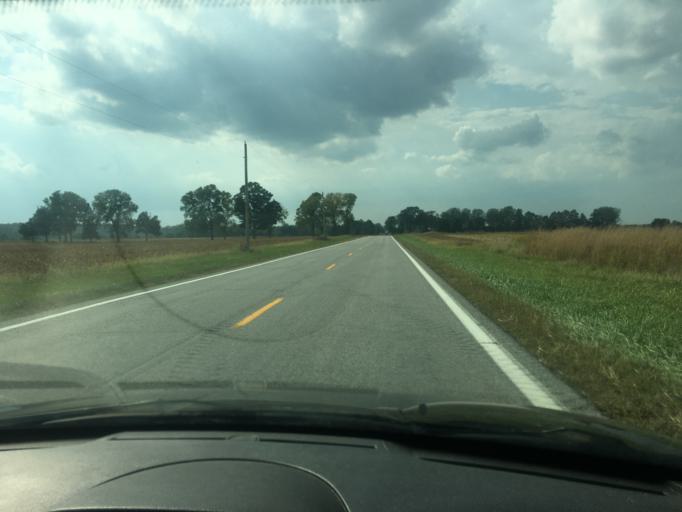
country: US
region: Ohio
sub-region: Champaign County
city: Urbana
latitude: 40.1560
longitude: -83.7565
